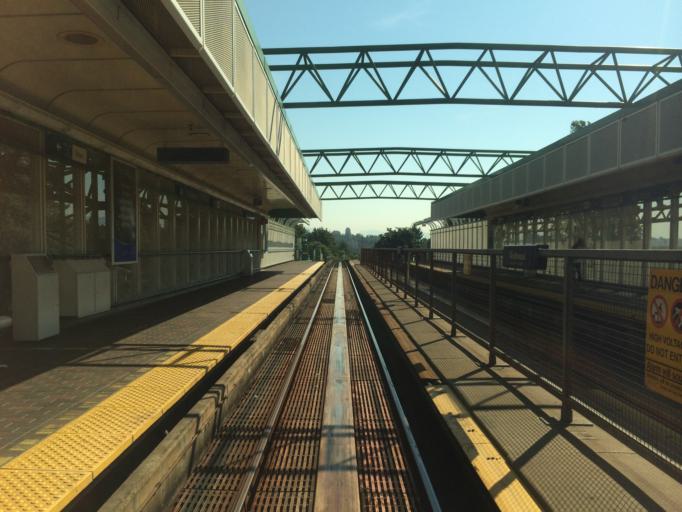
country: CA
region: British Columbia
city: New Westminster
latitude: 49.2001
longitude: -122.9487
